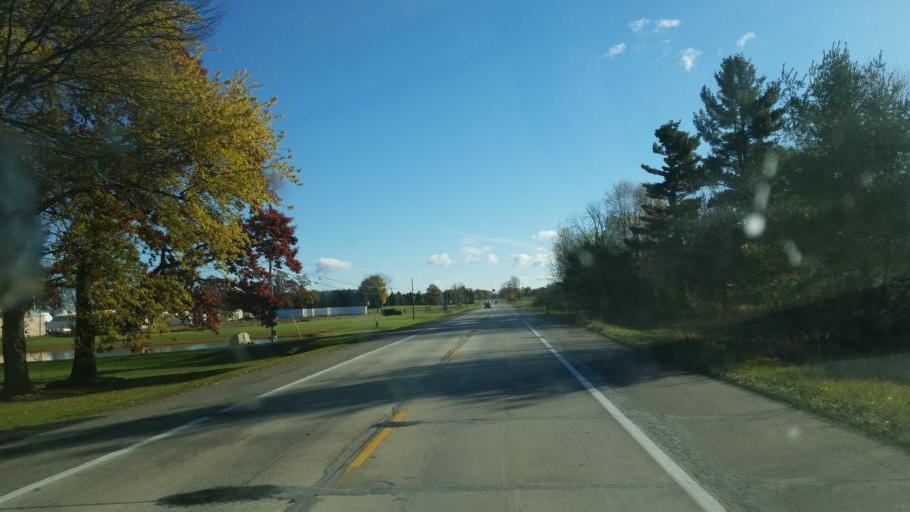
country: US
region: Michigan
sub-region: Montcalm County
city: Edmore
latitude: 43.4080
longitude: -85.0678
